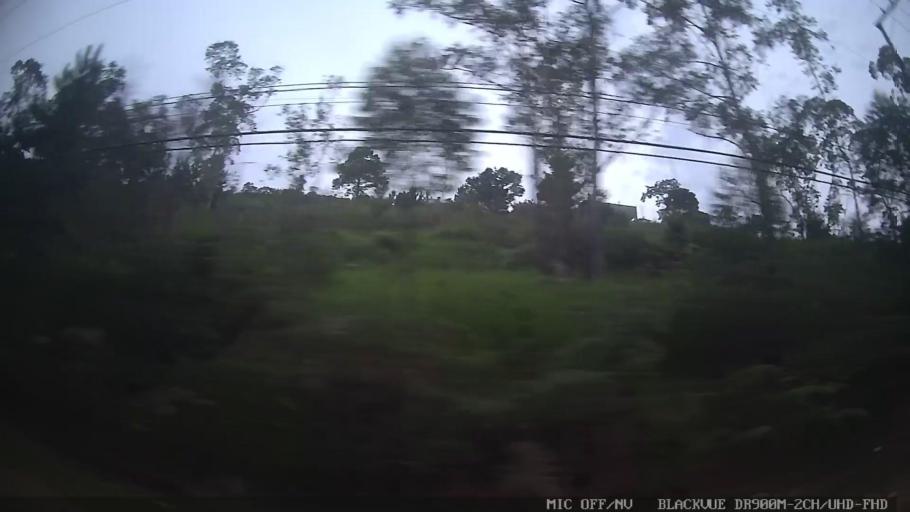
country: BR
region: Sao Paulo
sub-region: Rio Grande Da Serra
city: Rio Grande da Serra
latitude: -23.6933
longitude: -46.3056
